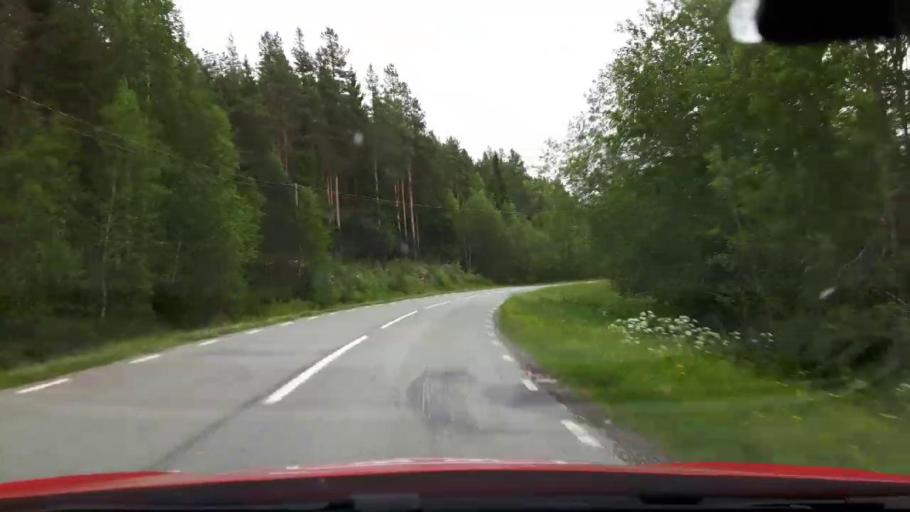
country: SE
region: Jaemtland
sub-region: Stroemsunds Kommun
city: Stroemsund
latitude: 63.4106
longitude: 15.6154
